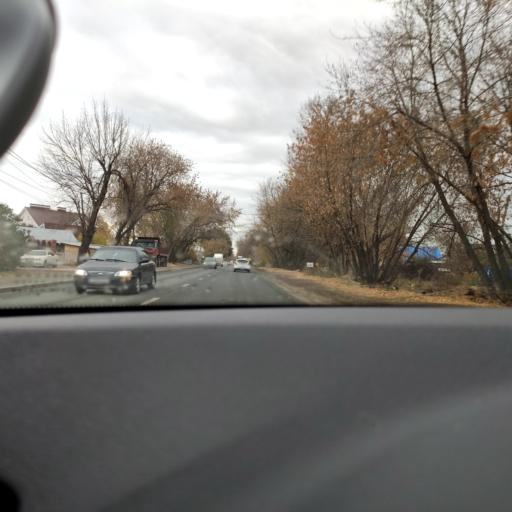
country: RU
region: Samara
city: Smyshlyayevka
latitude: 53.2333
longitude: 50.3106
